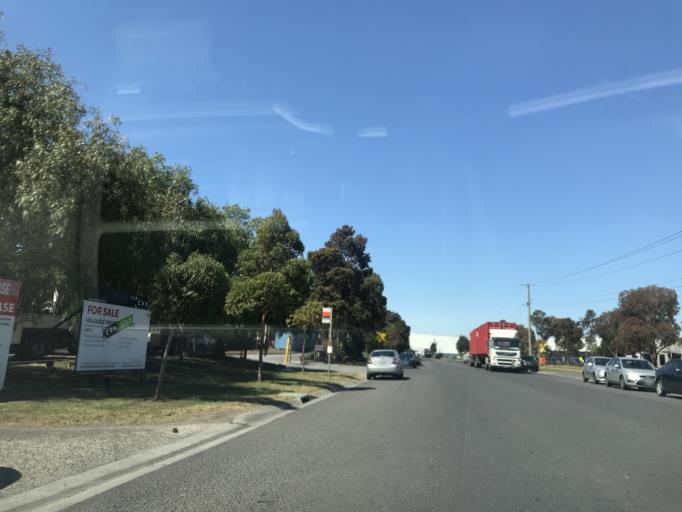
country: AU
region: Victoria
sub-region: Brimbank
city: Derrimut
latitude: -37.8168
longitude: 144.7792
